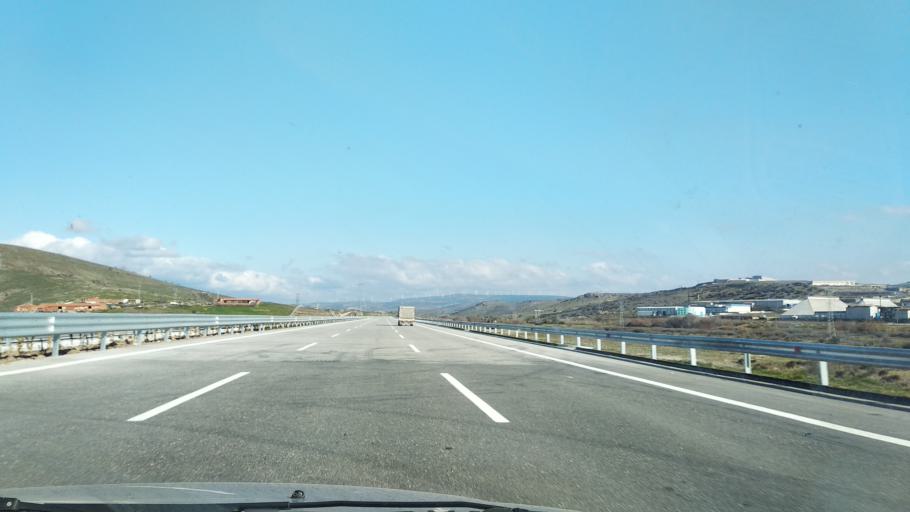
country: TR
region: Izmir
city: Yenisakran
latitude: 38.8265
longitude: 27.0354
